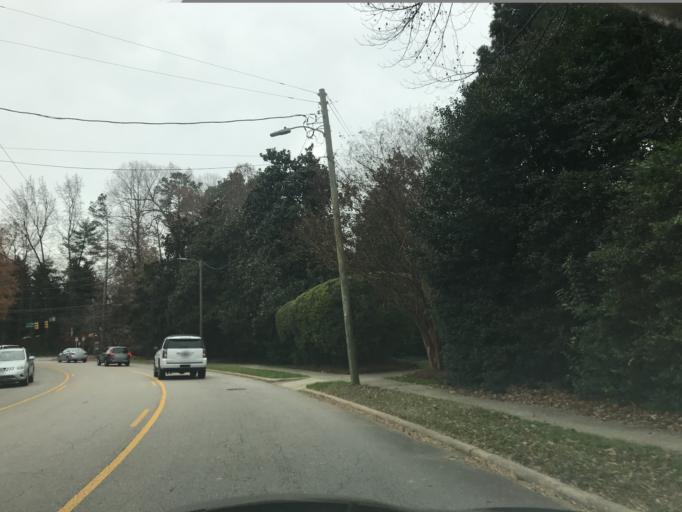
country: US
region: North Carolina
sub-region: Wake County
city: West Raleigh
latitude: 35.8235
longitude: -78.6510
